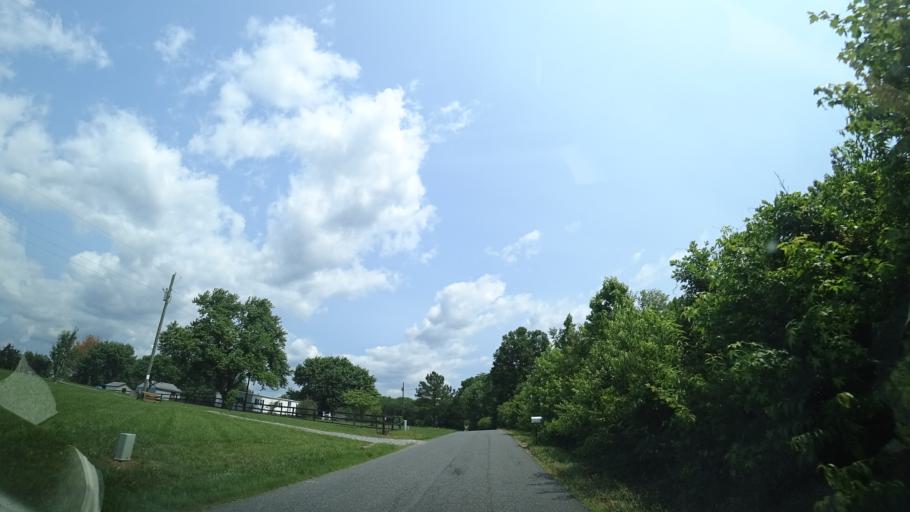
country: US
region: Virginia
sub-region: Spotsylvania County
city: Spotsylvania
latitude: 38.1188
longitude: -77.7908
